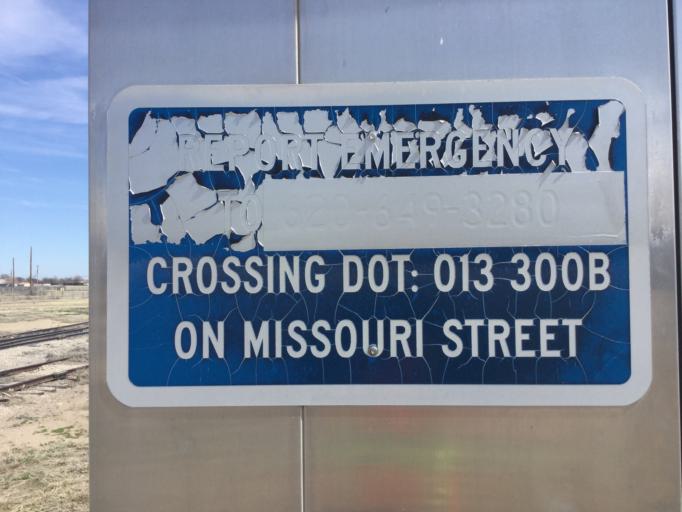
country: US
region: Kansas
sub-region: Grant County
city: Ulysses
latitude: 37.5791
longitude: -101.3542
